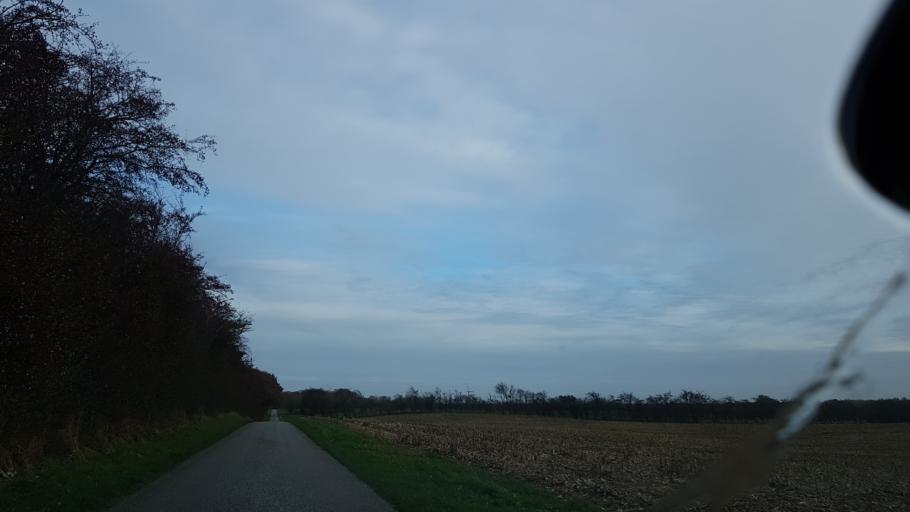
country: DK
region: South Denmark
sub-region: Haderslev Kommune
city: Vojens
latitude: 55.2998
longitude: 9.2556
